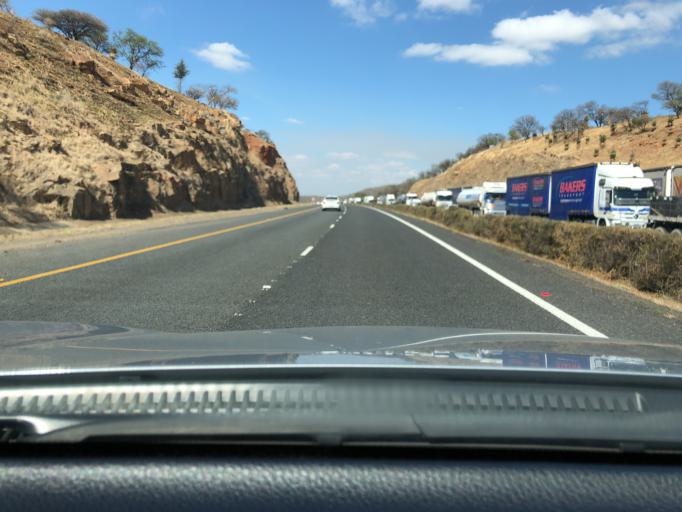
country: ZA
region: KwaZulu-Natal
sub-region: uThukela District Municipality
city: Ladysmith
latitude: -28.7282
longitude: 29.6458
